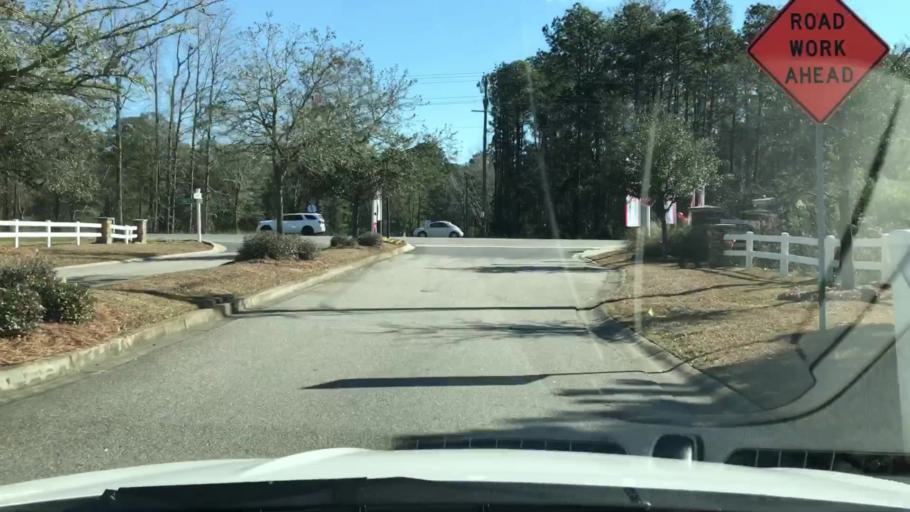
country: US
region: South Carolina
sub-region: Horry County
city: Garden City
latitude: 33.6406
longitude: -79.0313
